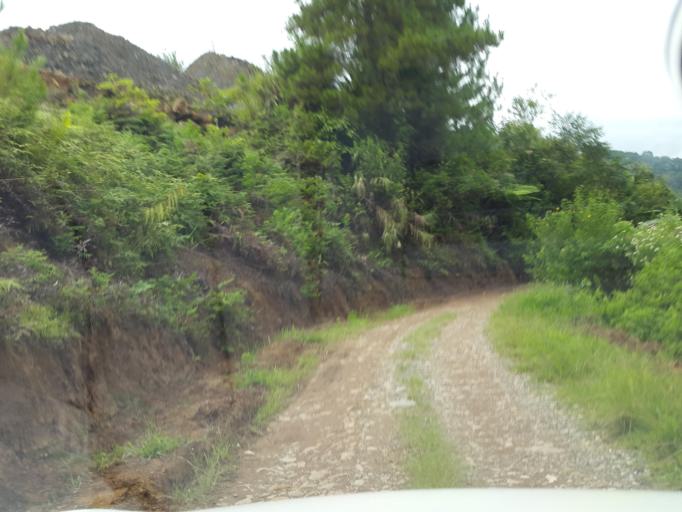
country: ID
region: South Sulawesi
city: Rantepang
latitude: -2.8621
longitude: 119.9522
